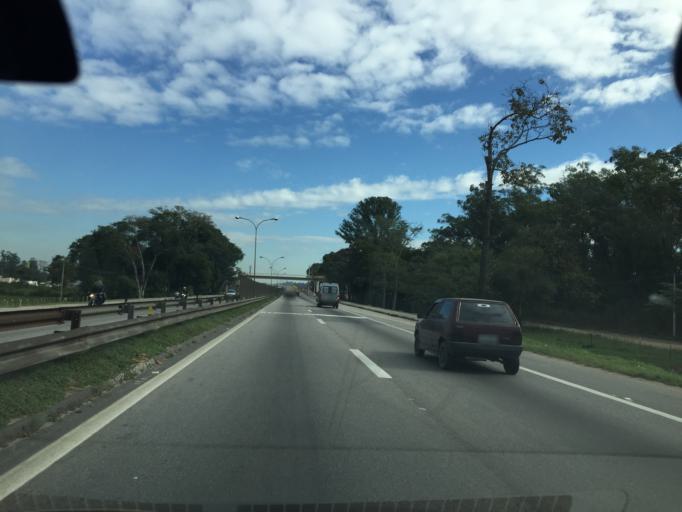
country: BR
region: Sao Paulo
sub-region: Jacarei
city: Jacarei
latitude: -23.2732
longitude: -45.9714
